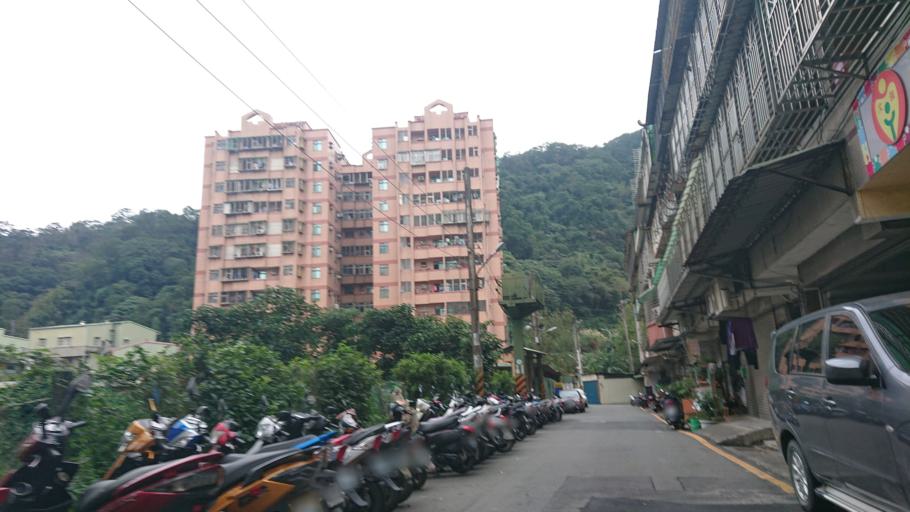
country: TW
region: Taiwan
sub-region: Taoyuan
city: Taoyuan
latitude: 24.9371
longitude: 121.3624
